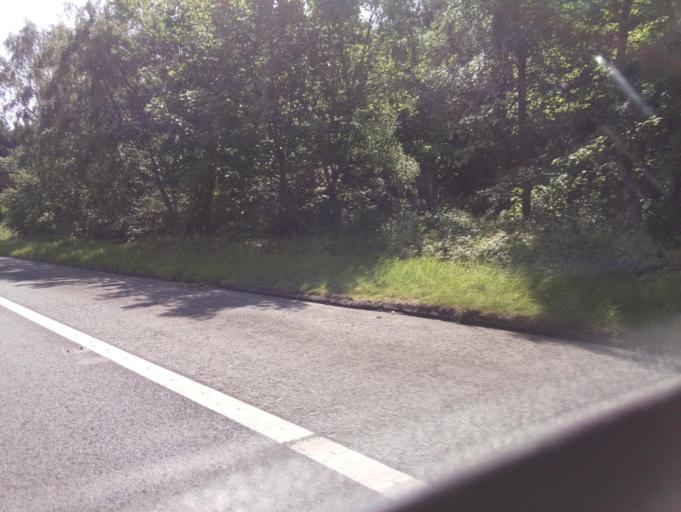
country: GB
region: England
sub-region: North Lincolnshire
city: Broughton
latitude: 53.5473
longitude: -0.5791
